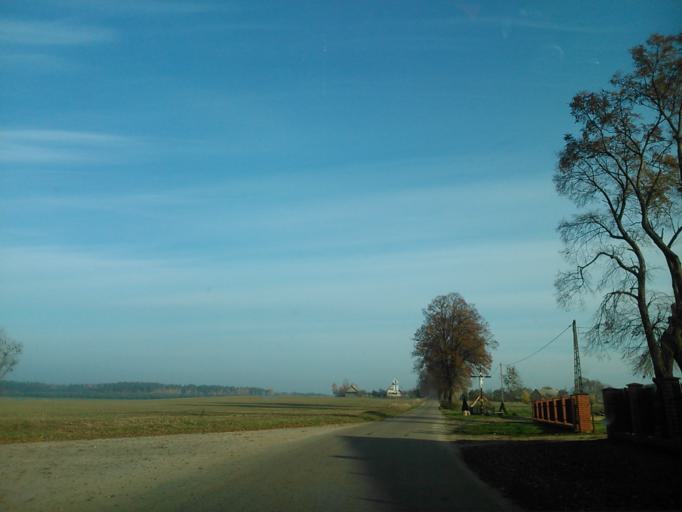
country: PL
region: Warmian-Masurian Voivodeship
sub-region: Powiat dzialdowski
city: Rybno
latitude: 53.2766
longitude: 19.9652
